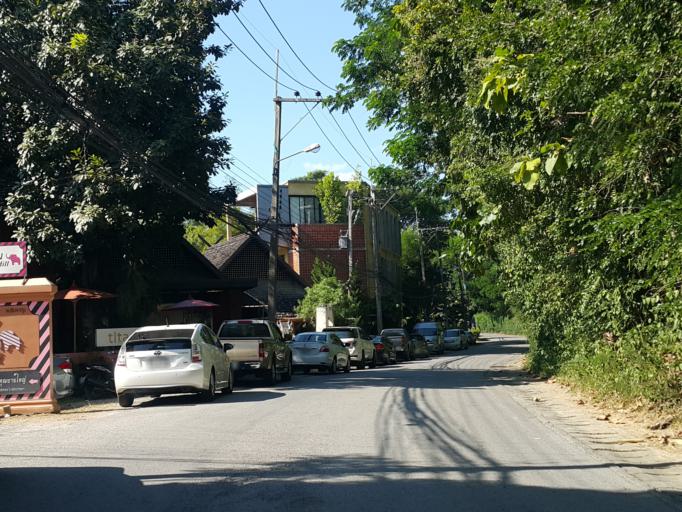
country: TH
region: Chiang Mai
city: San Sai
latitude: 18.9134
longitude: 98.9302
